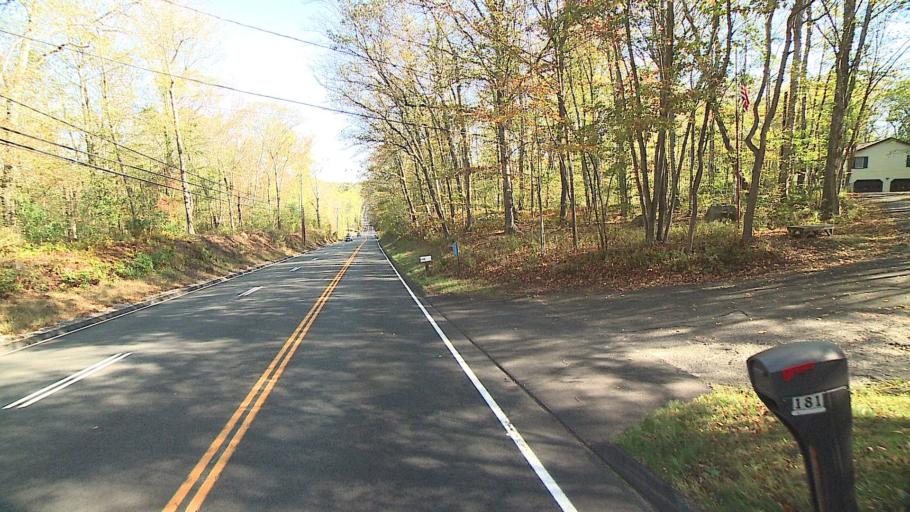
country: US
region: Connecticut
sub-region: Hartford County
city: Terramuggus
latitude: 41.6115
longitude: -72.4773
